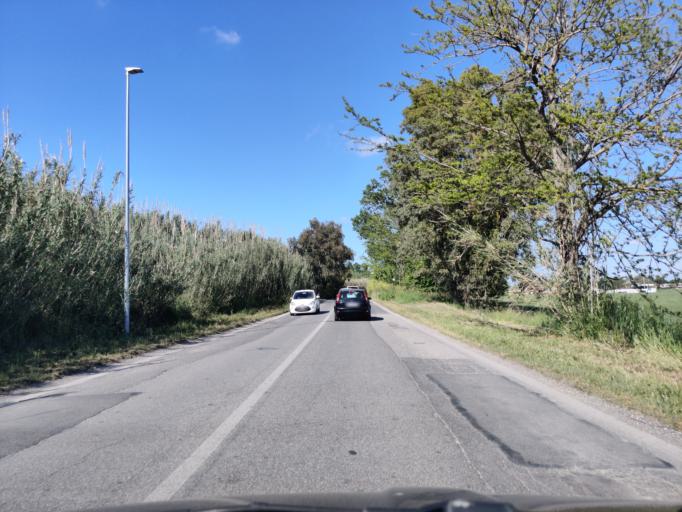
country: IT
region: Latium
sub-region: Citta metropolitana di Roma Capitale
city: Maccarese
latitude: 41.8745
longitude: 12.2105
